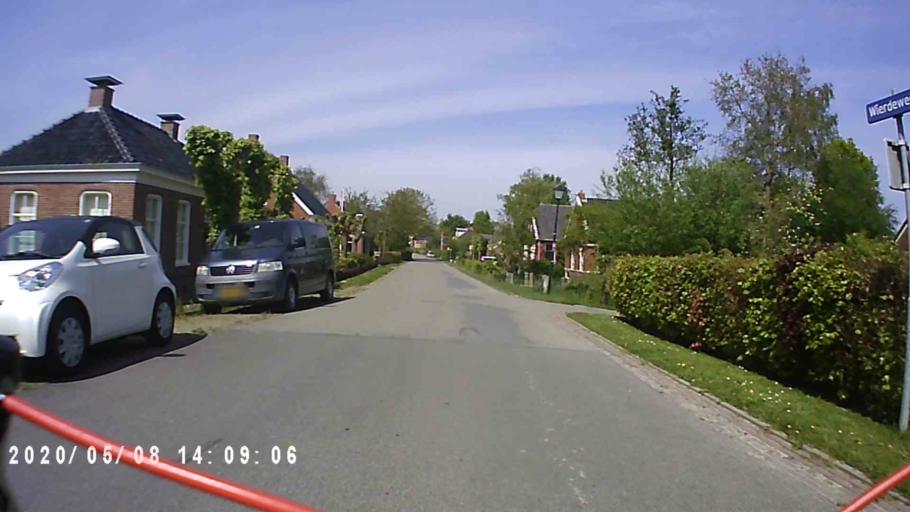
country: NL
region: Groningen
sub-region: Gemeente Appingedam
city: Appingedam
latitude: 53.3439
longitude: 6.7996
